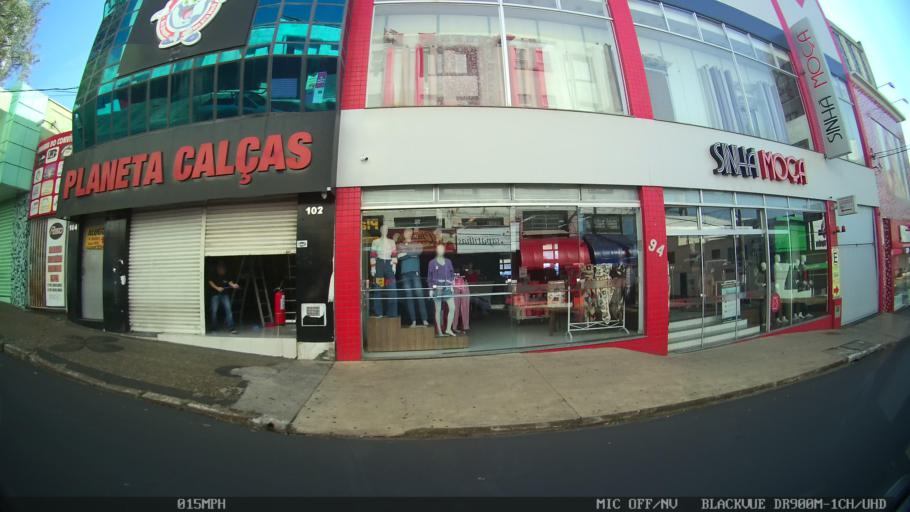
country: BR
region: Sao Paulo
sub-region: Americana
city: Americana
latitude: -22.7394
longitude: -47.3294
